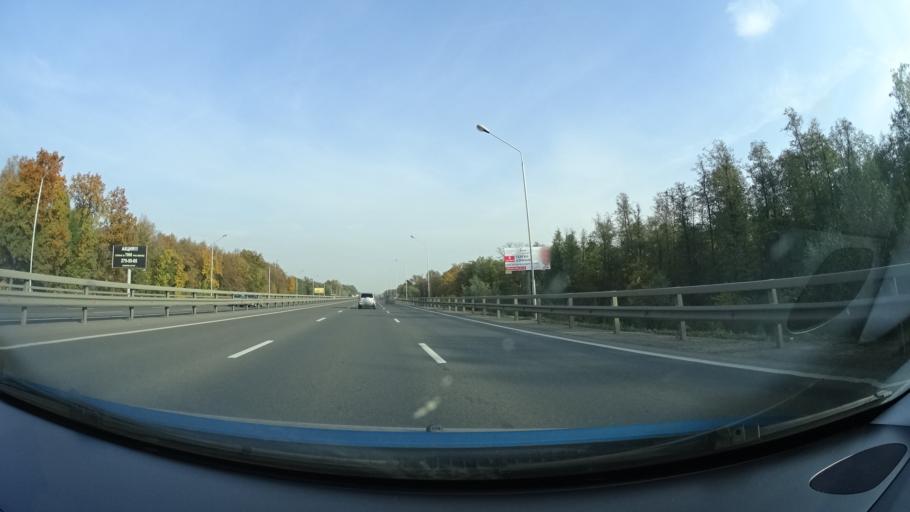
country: RU
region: Bashkortostan
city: Avdon
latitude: 54.6667
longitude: 55.8528
